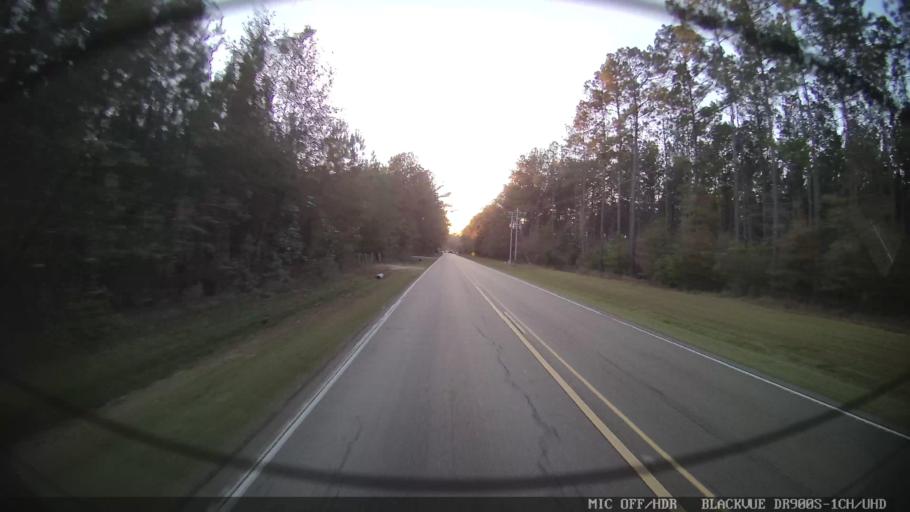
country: US
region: Mississippi
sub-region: Stone County
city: Wiggins
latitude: 31.0481
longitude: -89.2047
